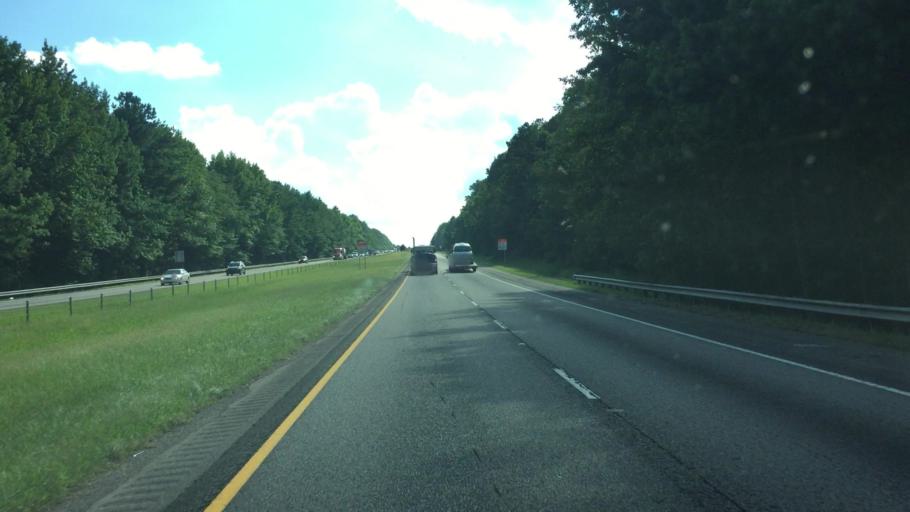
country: US
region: Georgia
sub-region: Barrow County
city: Auburn
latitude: 34.0821
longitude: -83.8748
